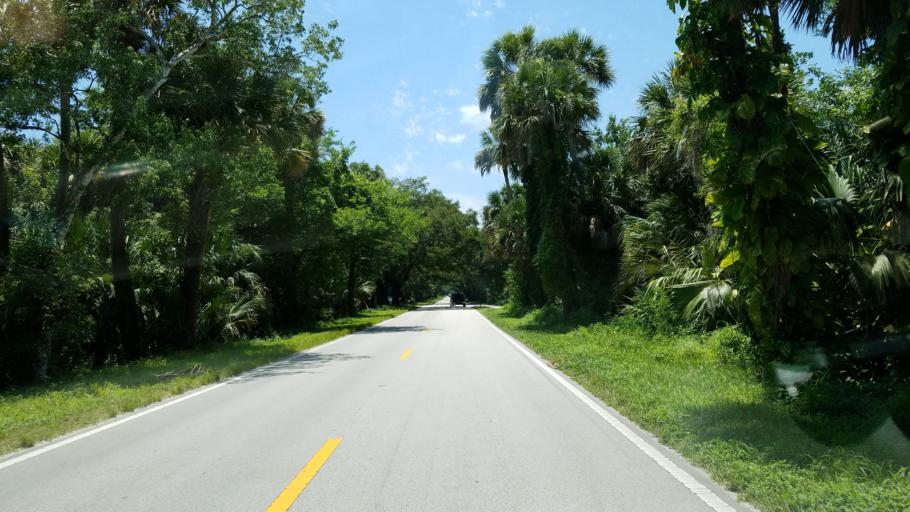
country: US
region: Florida
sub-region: Martin County
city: Indiantown
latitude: 27.1622
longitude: -80.5706
